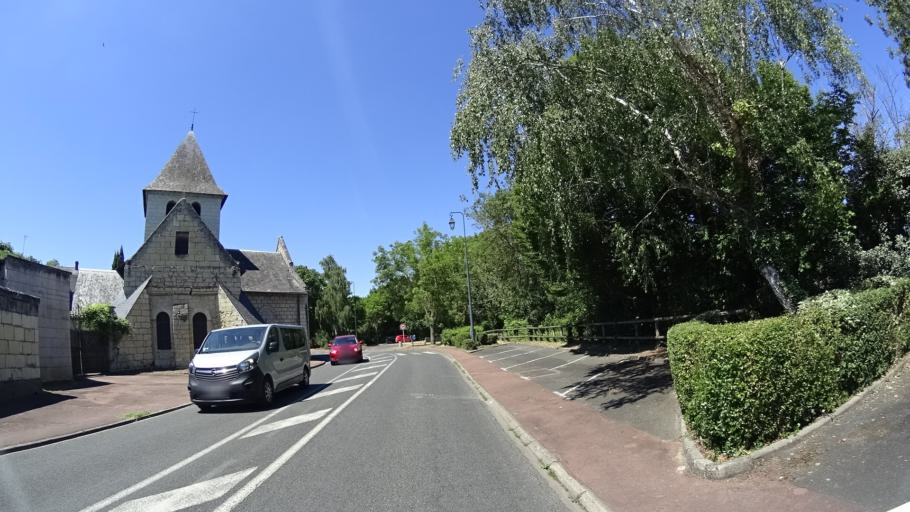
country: FR
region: Pays de la Loire
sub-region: Departement de Maine-et-Loire
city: Saumur
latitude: 47.2744
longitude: -0.1092
